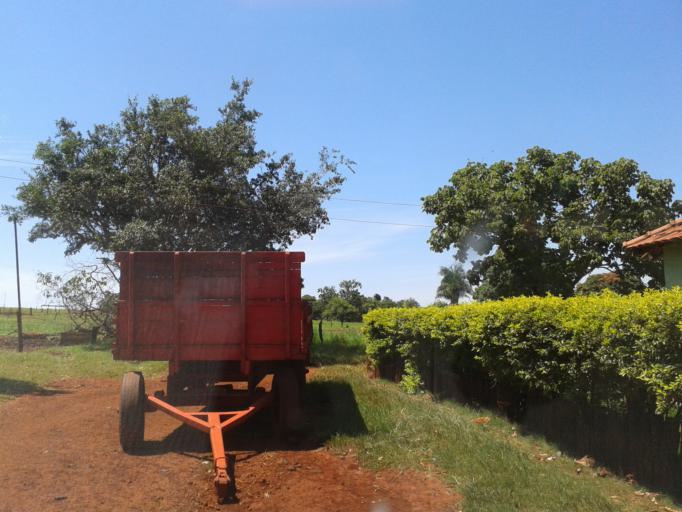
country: BR
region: Minas Gerais
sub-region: Centralina
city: Centralina
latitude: -18.6302
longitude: -49.2951
